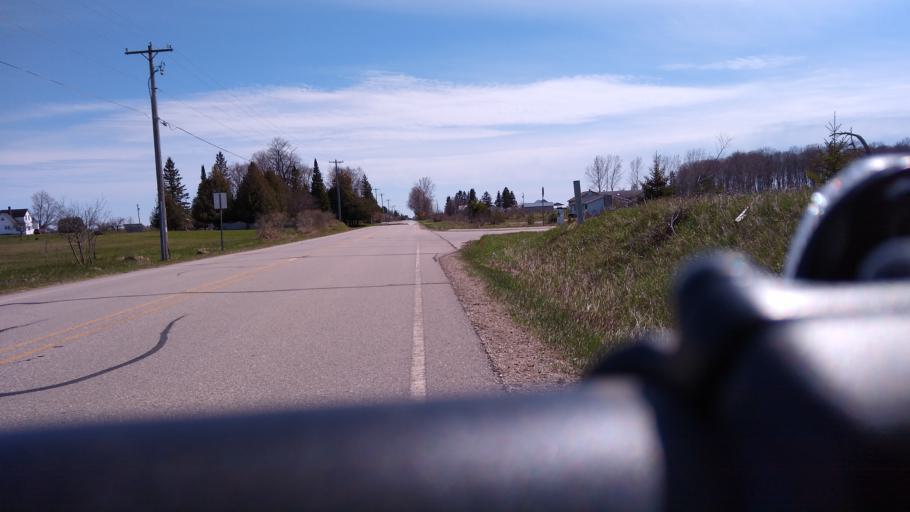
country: US
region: Michigan
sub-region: Delta County
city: Escanaba
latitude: 45.7197
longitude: -87.2025
